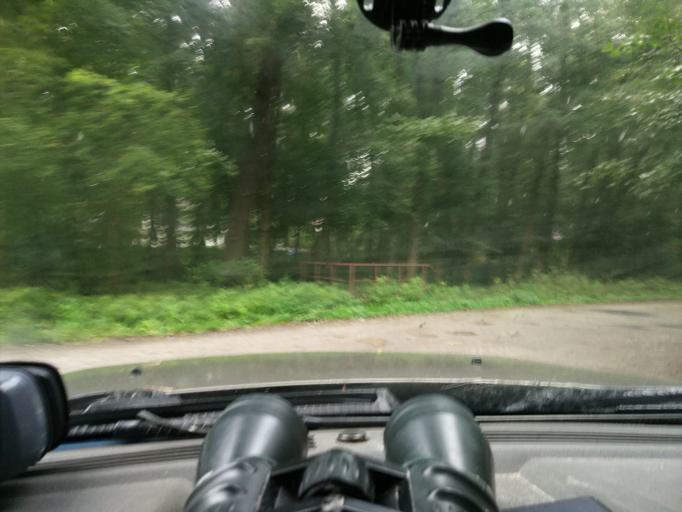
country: PL
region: Masovian Voivodeship
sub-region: Powiat grodziski
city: Podkowa Lesna
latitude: 52.1263
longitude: 20.7354
